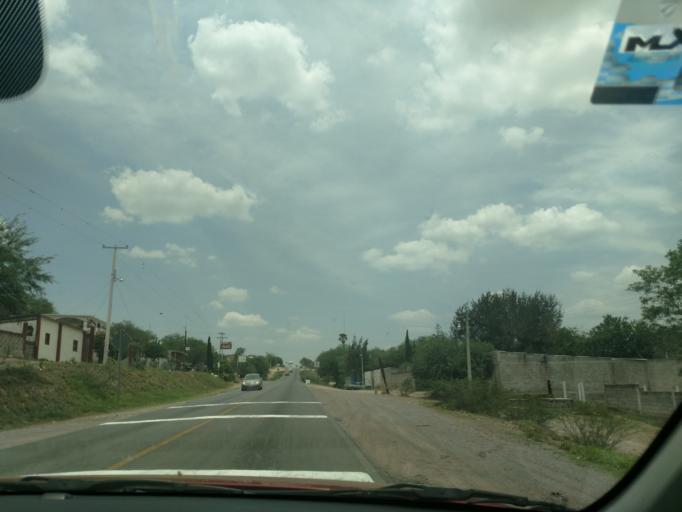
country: MX
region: San Luis Potosi
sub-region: Rioverde
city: Progreso
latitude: 22.0191
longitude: -100.3760
